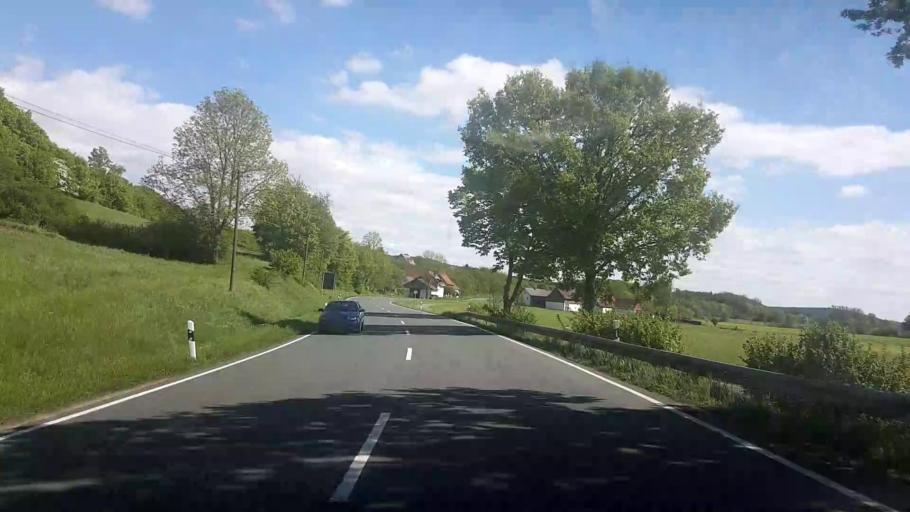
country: DE
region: Bavaria
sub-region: Upper Franconia
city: Rattelsdorf
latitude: 50.0645
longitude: 10.8714
